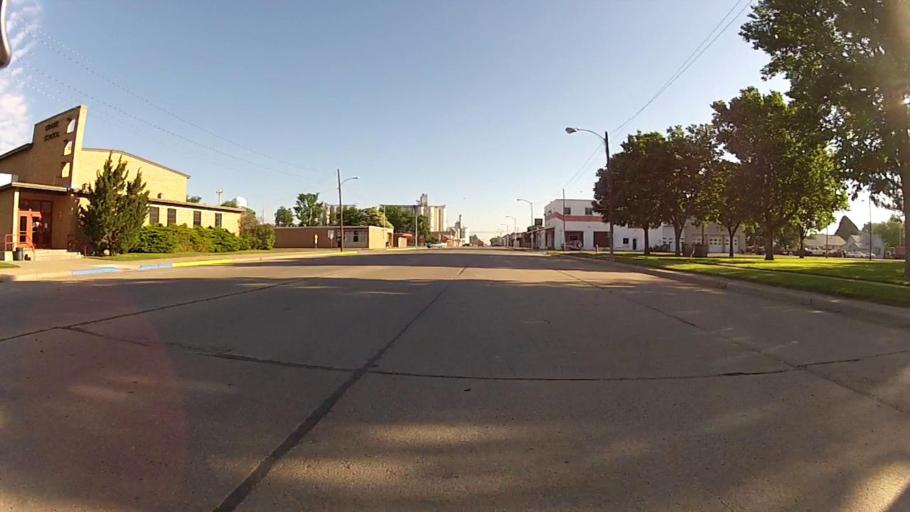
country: US
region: Kansas
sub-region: Haskell County
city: Sublette
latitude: 37.4795
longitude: -100.8439
